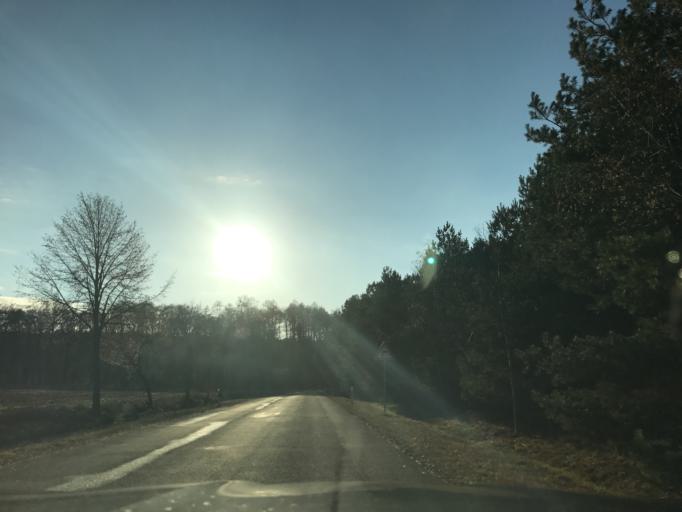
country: DE
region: Saxony-Anhalt
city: Loburg
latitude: 52.1737
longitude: 12.0399
